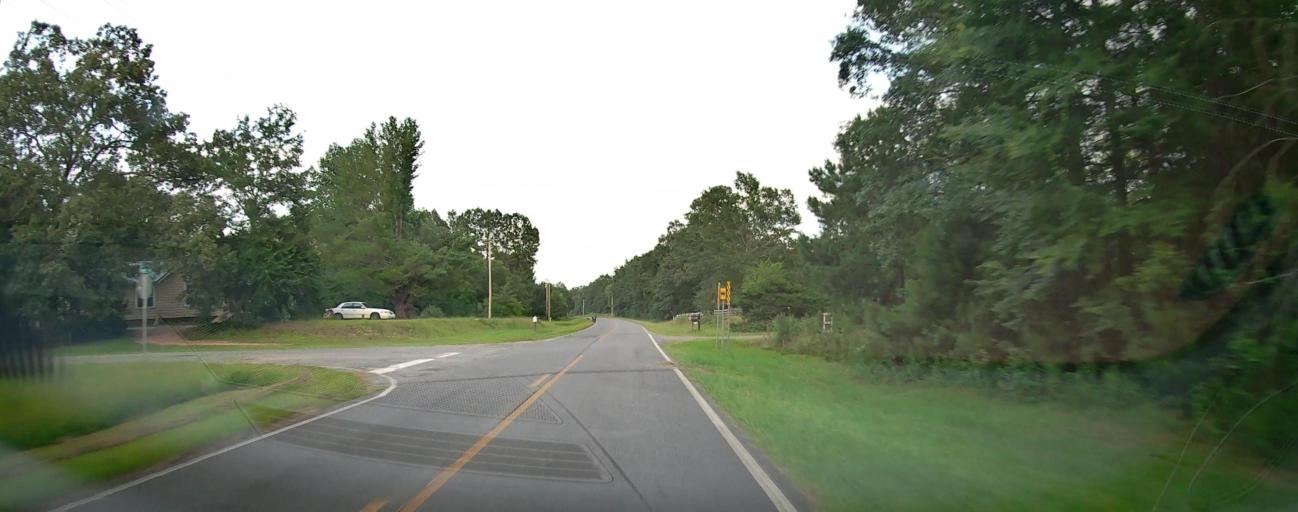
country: US
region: Georgia
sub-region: Crawford County
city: Roberta
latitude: 32.6549
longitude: -84.0465
